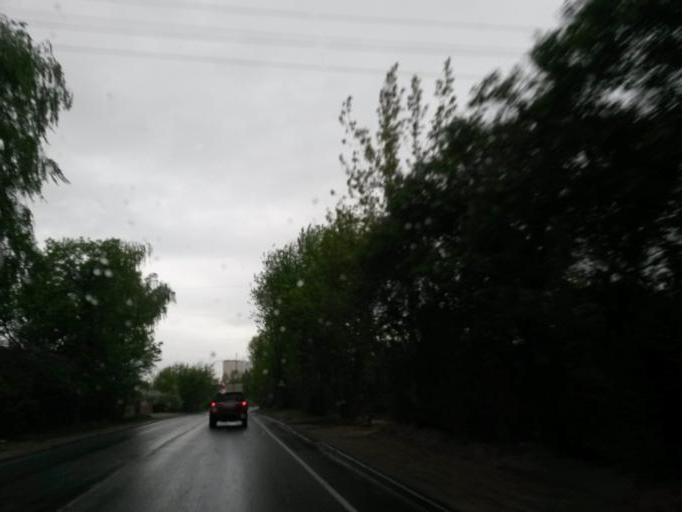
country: RU
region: Moskovskaya
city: Yam
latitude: 55.4647
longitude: 37.7015
